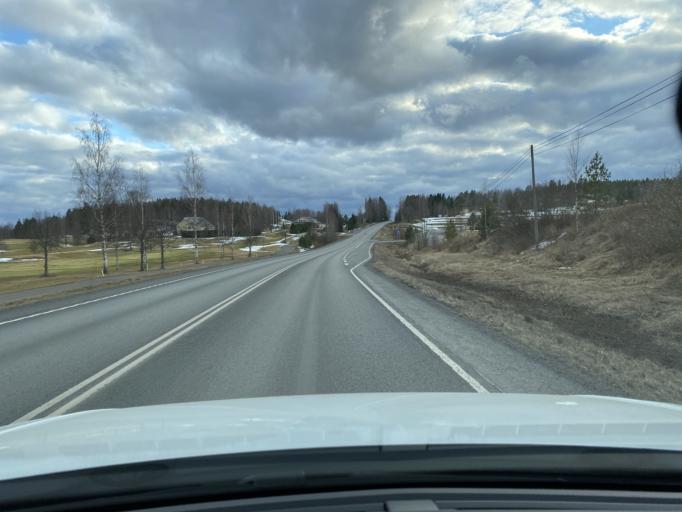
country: FI
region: Pirkanmaa
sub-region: Lounais-Pirkanmaa
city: Mouhijaervi
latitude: 61.4255
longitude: 23.0038
